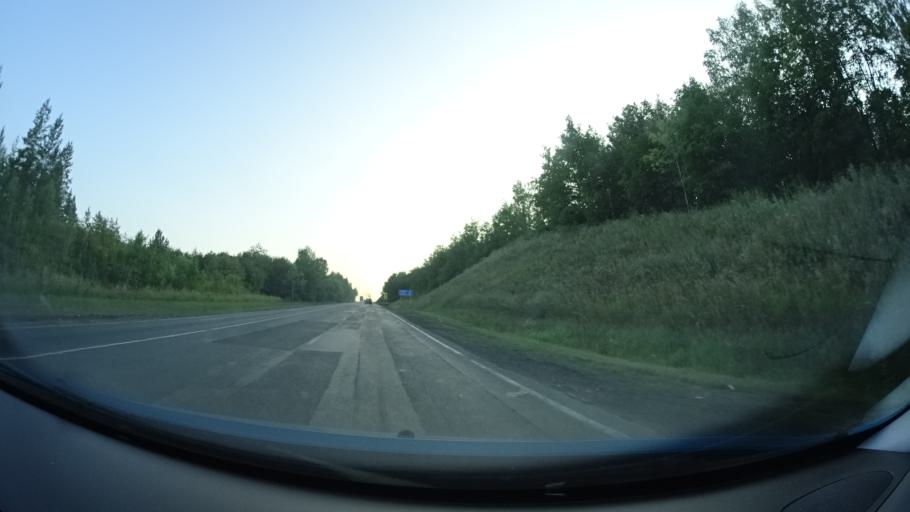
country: RU
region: Samara
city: Isakly
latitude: 53.9953
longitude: 51.5385
